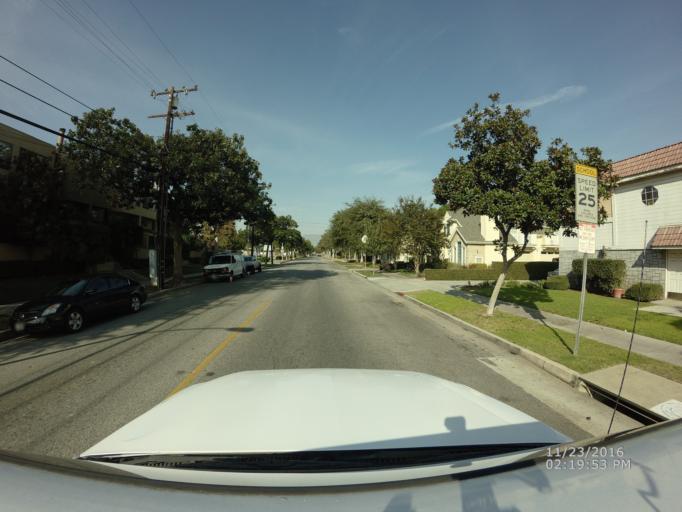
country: US
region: California
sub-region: Los Angeles County
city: Alhambra
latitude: 34.0944
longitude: -118.1421
